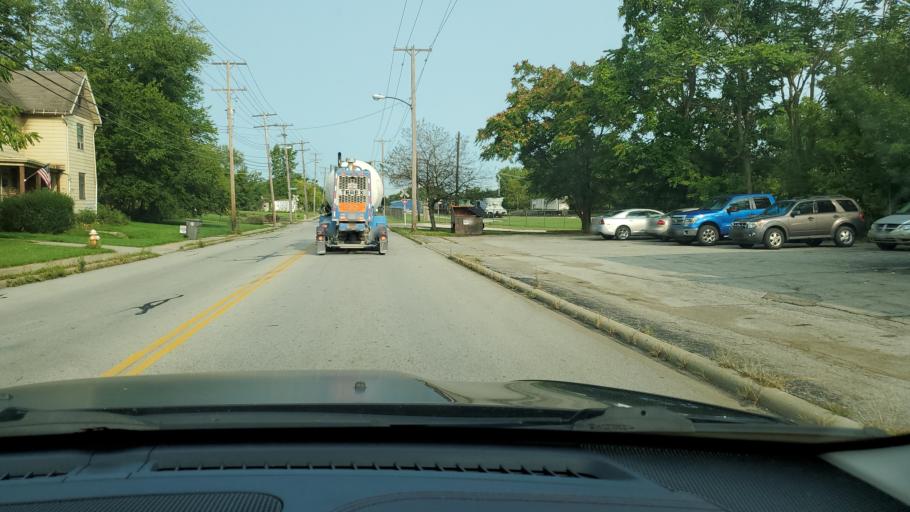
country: US
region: Ohio
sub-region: Mahoning County
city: Youngstown
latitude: 41.0799
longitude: -80.6288
